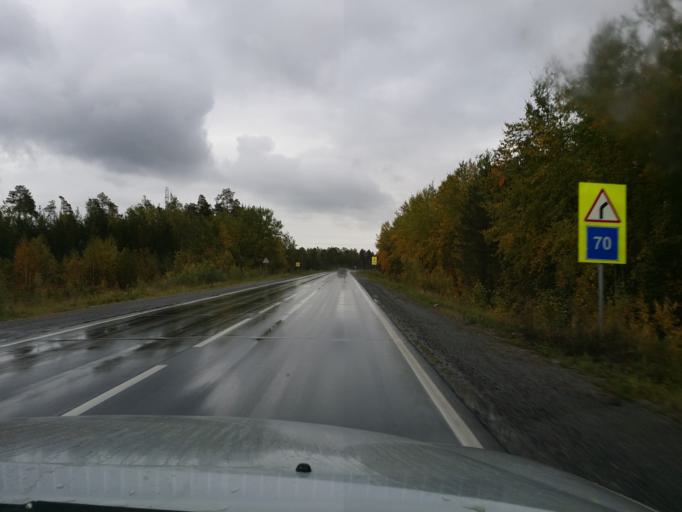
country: RU
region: Khanty-Mansiyskiy Avtonomnyy Okrug
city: Megion
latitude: 61.1260
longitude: 75.8176
